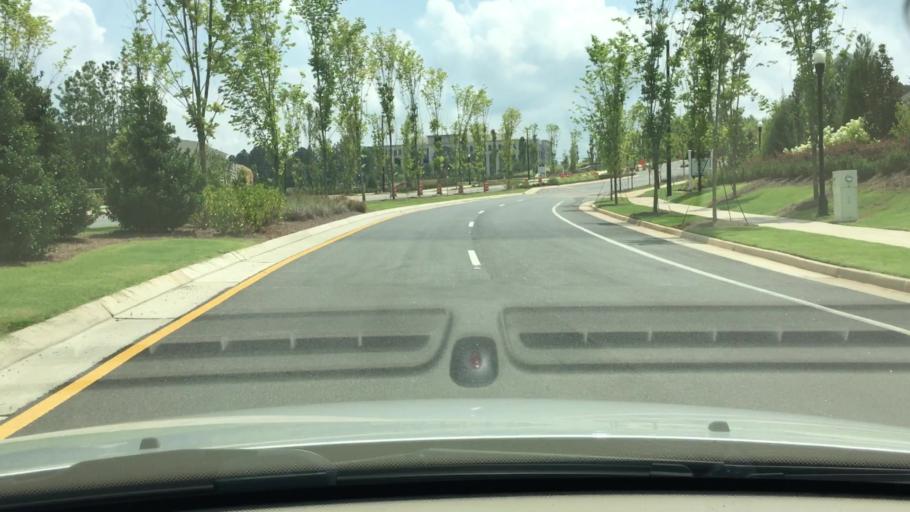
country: US
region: Georgia
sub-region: Fulton County
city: Alpharetta
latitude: 34.0645
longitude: -84.2765
